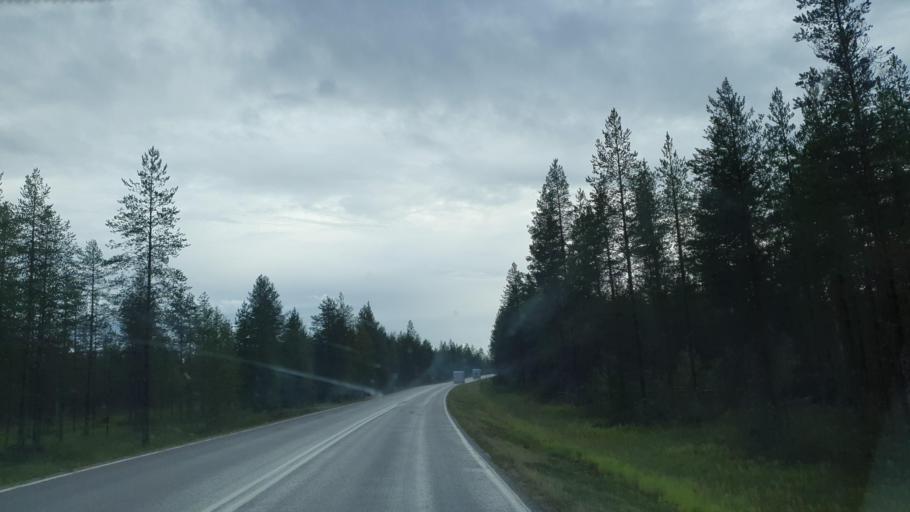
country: FI
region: Kainuu
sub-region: Kehys-Kainuu
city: Puolanka
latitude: 65.0573
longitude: 27.7155
